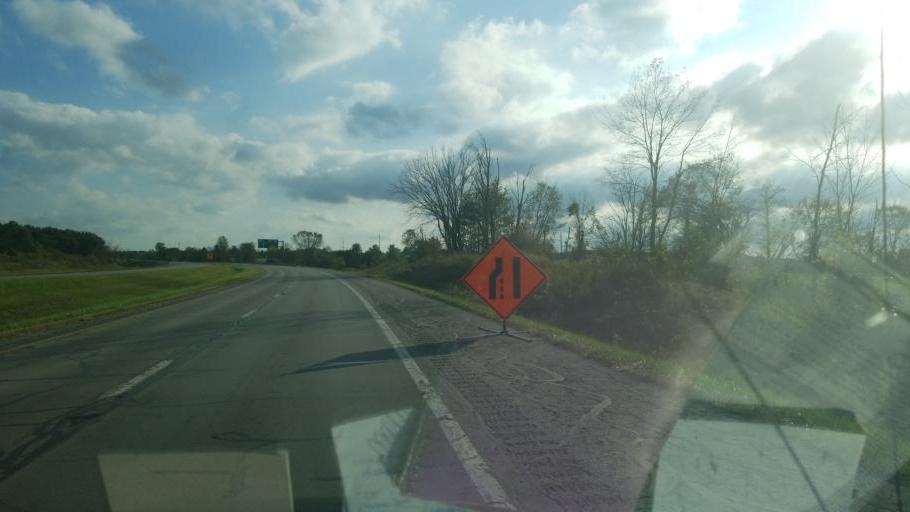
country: US
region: Ohio
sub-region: Medina County
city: Lodi
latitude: 41.0354
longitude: -82.0510
